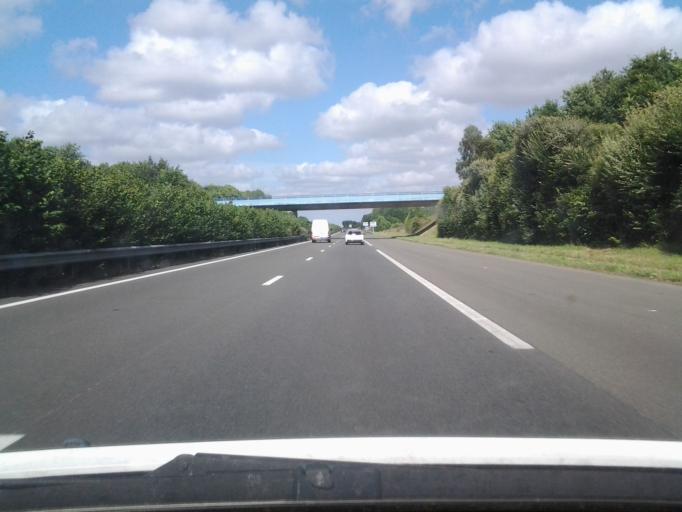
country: FR
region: Pays de la Loire
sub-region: Departement de la Vendee
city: Landeronde
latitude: 46.6349
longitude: -1.5543
